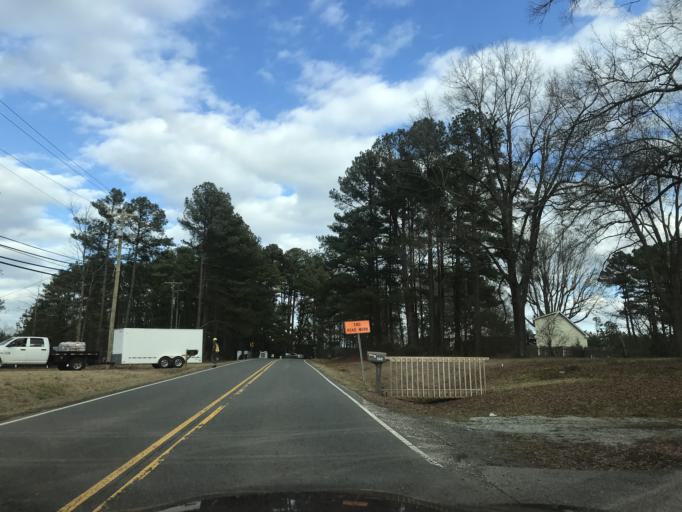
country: US
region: North Carolina
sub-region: Durham County
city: Durham
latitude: 35.9677
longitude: -78.8409
